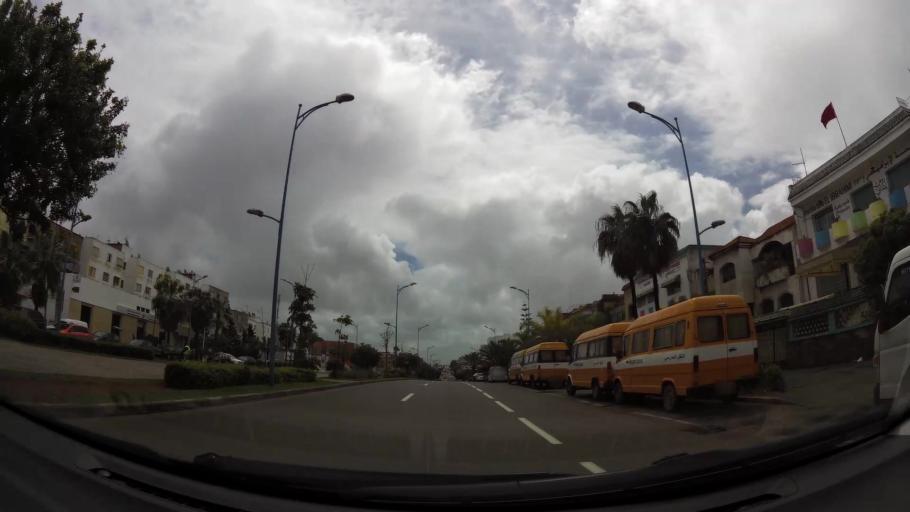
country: MA
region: Grand Casablanca
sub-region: Casablanca
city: Casablanca
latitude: 33.5561
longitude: -7.6819
